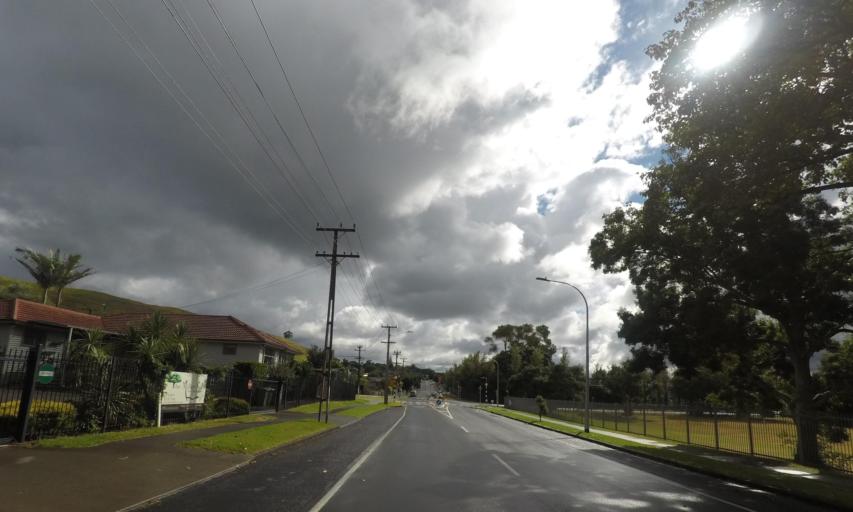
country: NZ
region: Auckland
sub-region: Auckland
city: Mangere
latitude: -36.9560
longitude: 174.7847
